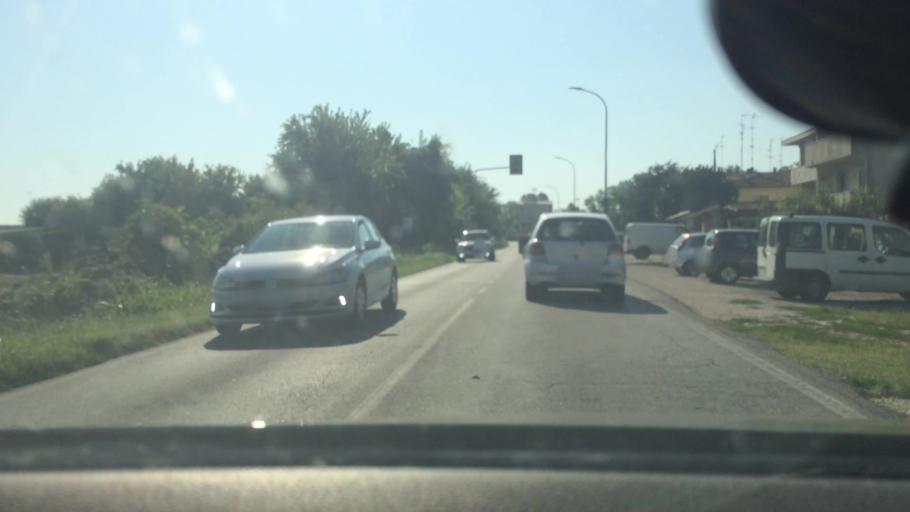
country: IT
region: Emilia-Romagna
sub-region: Provincia di Ferrara
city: Comacchio
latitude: 44.6935
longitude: 12.1928
